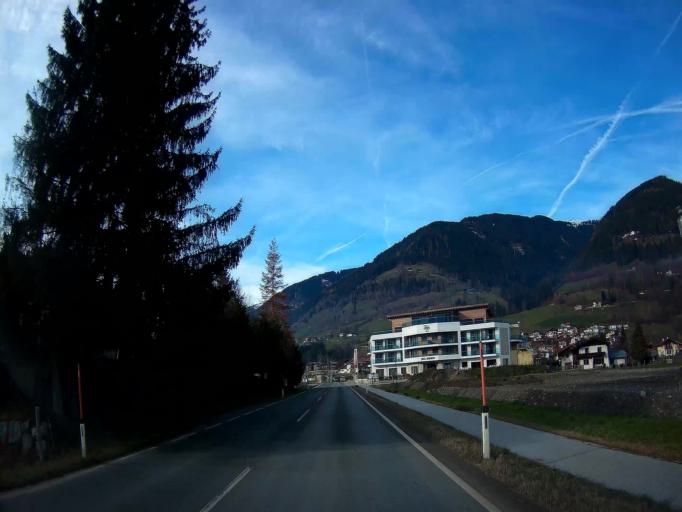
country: AT
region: Salzburg
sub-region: Politischer Bezirk Zell am See
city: Kaprun
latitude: 47.2869
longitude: 12.7482
